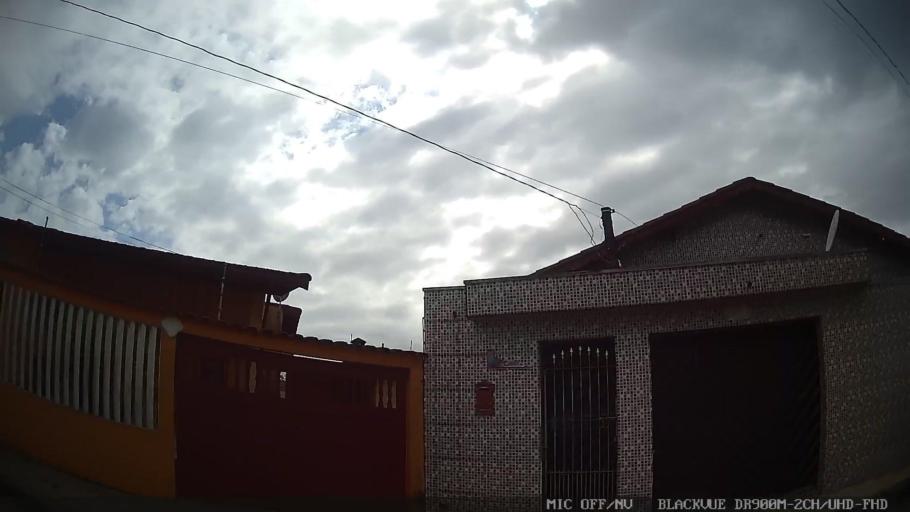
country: BR
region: Sao Paulo
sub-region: Itanhaem
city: Itanhaem
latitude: -24.1875
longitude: -46.8144
